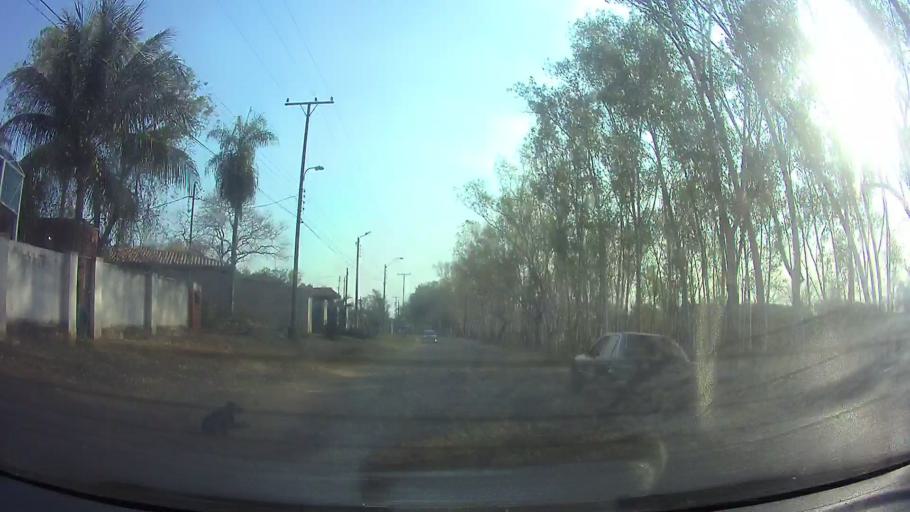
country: PY
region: Central
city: Limpio
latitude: -25.2224
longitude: -57.5055
